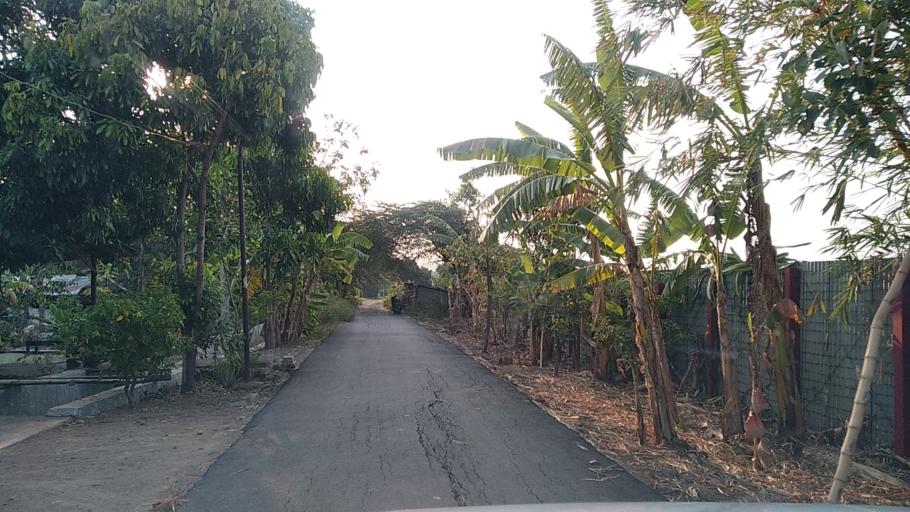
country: ID
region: Central Java
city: Semarang
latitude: -6.9686
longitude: 110.2967
